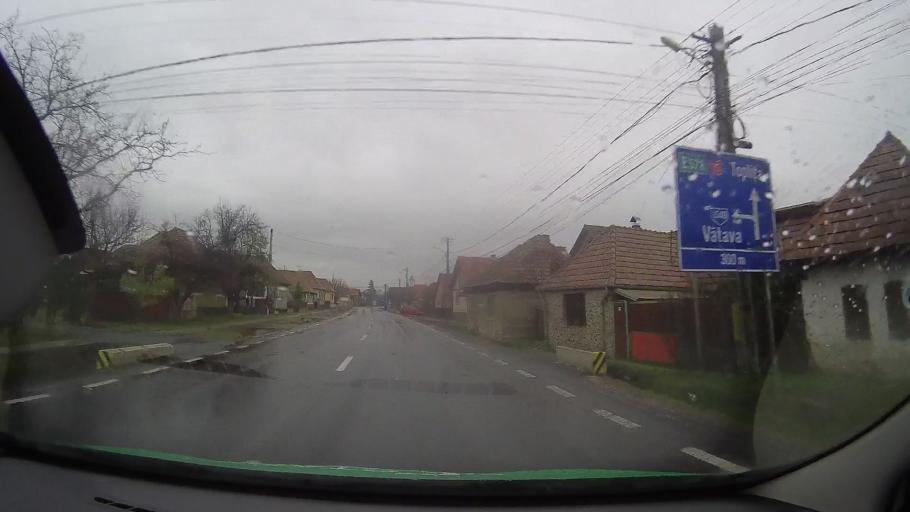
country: RO
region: Mures
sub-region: Comuna Brancovenesti
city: Valenii de Mures
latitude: 46.8889
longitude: 24.7948
